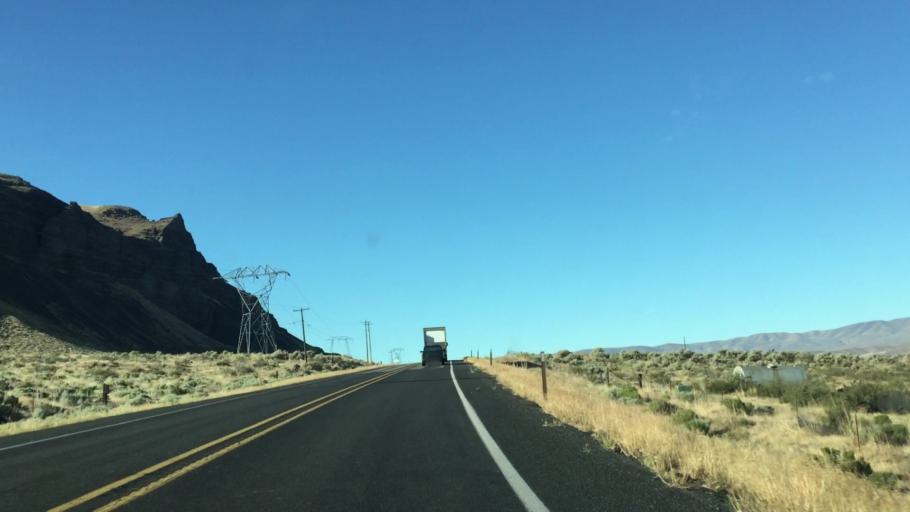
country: US
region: Washington
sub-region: Grant County
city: Mattawa
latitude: 46.8130
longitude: -119.9196
